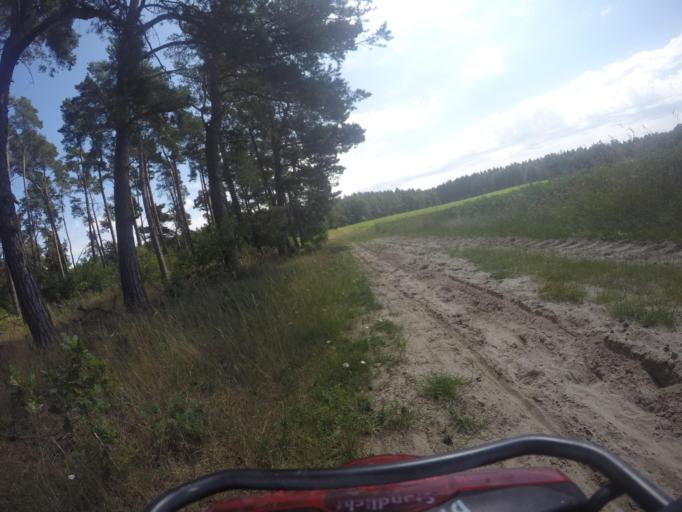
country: DE
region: Lower Saxony
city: Dahlem
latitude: 53.2230
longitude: 10.7303
